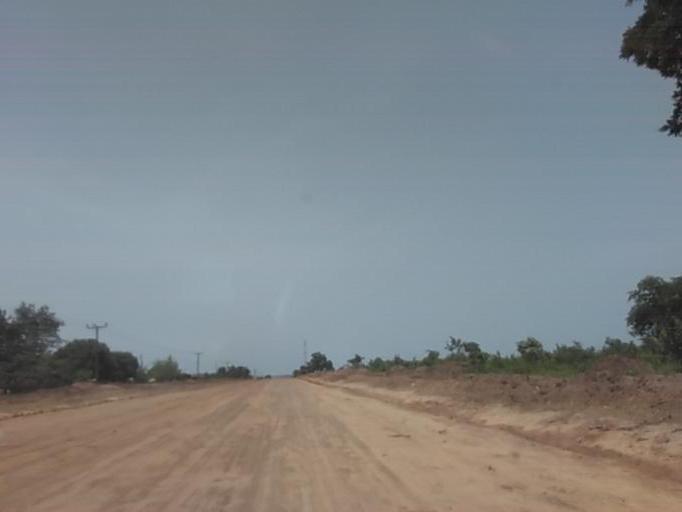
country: GH
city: Kpandae
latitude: 8.6385
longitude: 0.2222
